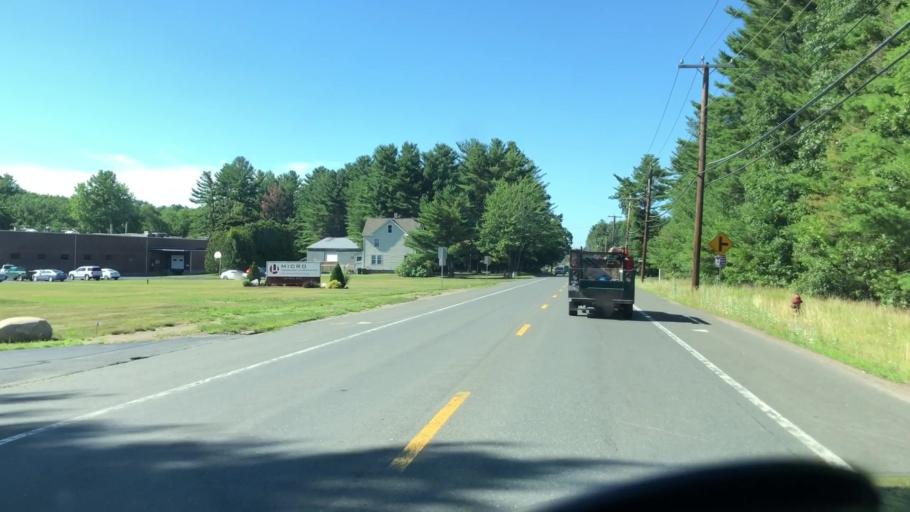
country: US
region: Massachusetts
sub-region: Hampden County
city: Westfield
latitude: 42.1640
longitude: -72.7264
